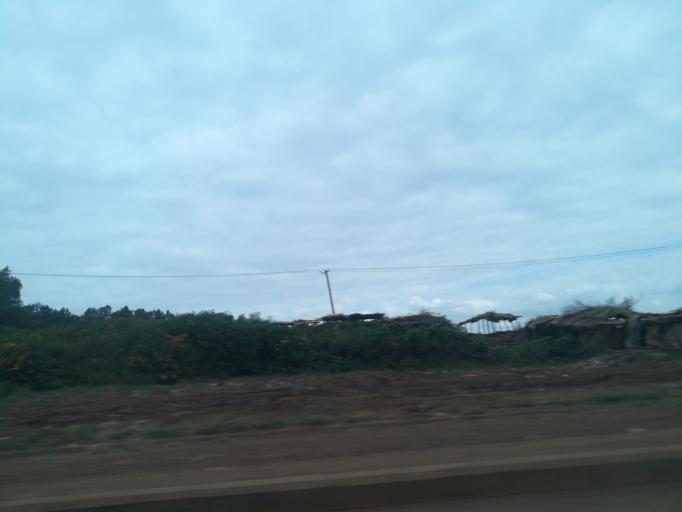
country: KE
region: Nairobi Area
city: Thika
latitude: -1.0831
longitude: 37.0416
